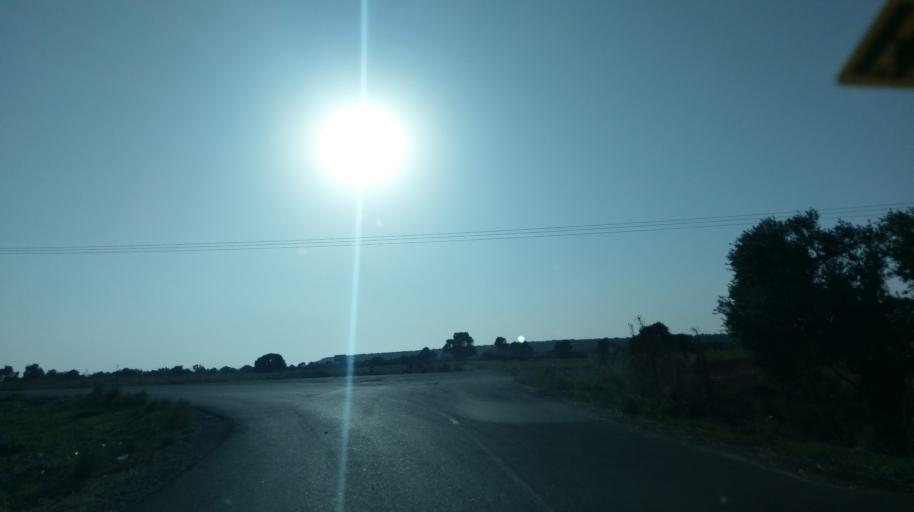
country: CY
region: Ammochostos
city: Leonarisso
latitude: 35.3348
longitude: 34.0620
